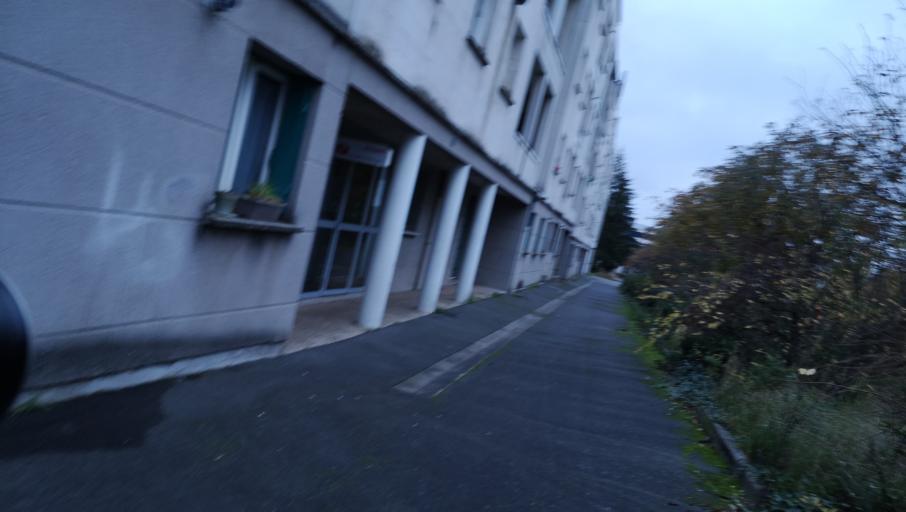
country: FR
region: Centre
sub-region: Departement du Loiret
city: Saint-Jean-le-Blanc
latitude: 47.9075
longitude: 1.9225
